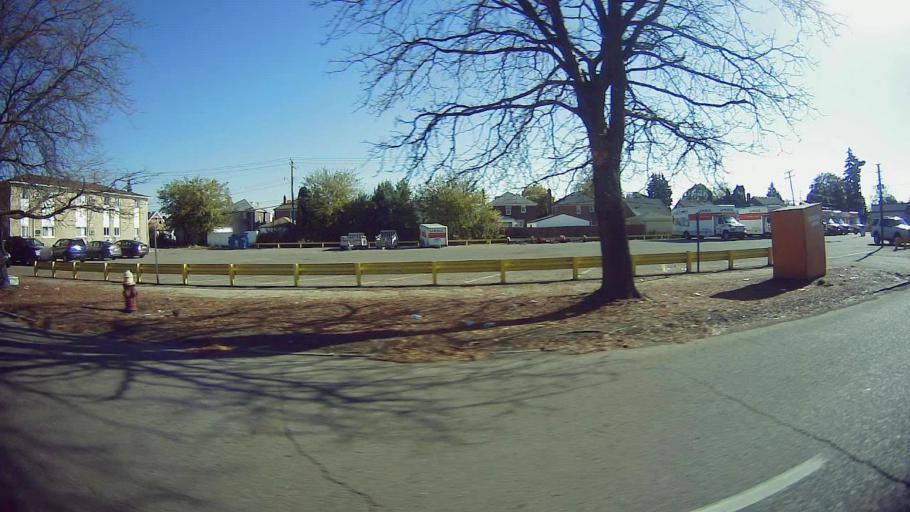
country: US
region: Michigan
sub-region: Wayne County
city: Dearborn
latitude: 42.3524
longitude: -83.1771
